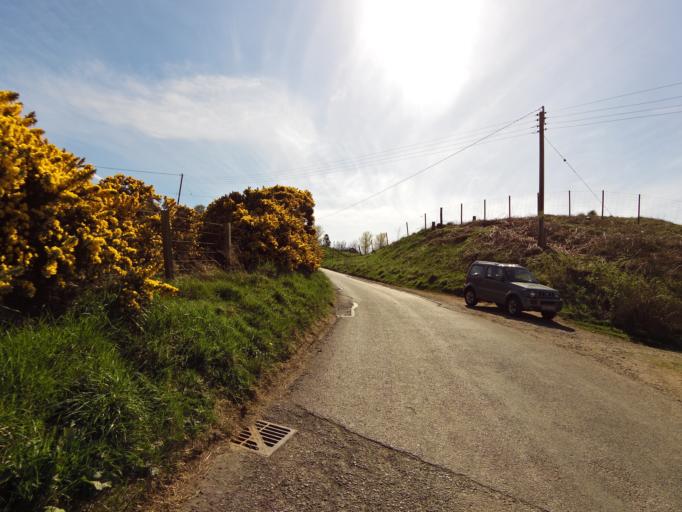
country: GB
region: Scotland
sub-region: Angus
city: Montrose
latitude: 56.6495
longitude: -2.5144
